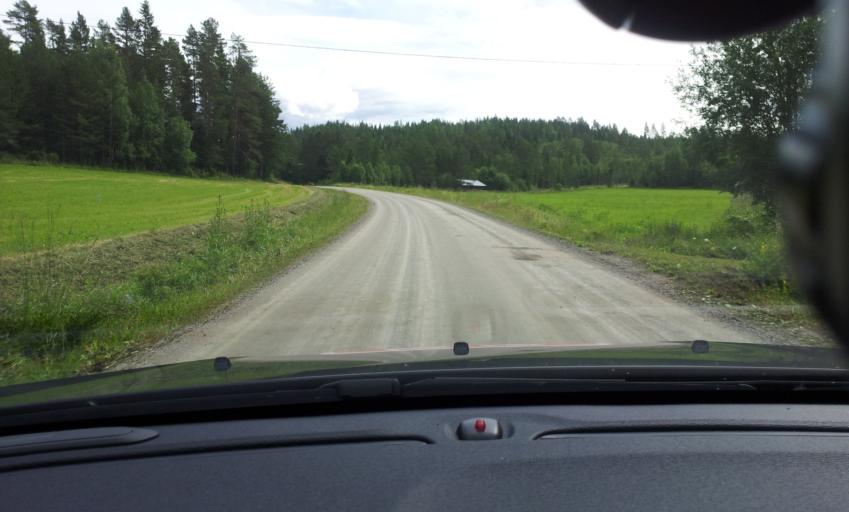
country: SE
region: Jaemtland
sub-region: OEstersunds Kommun
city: Brunflo
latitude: 62.9391
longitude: 14.9619
